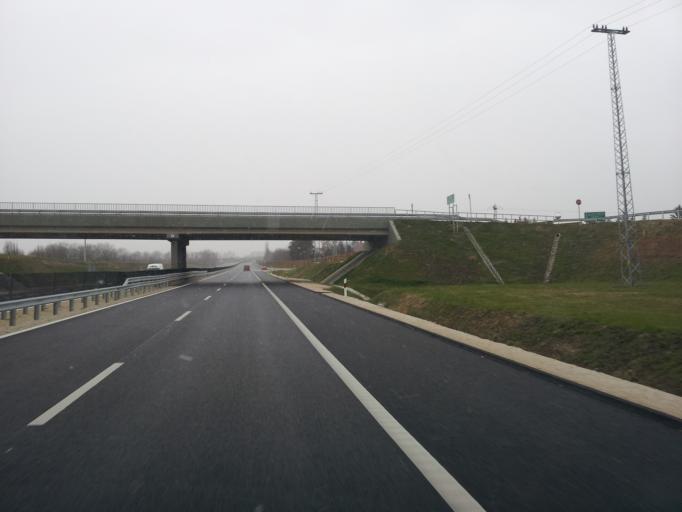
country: HU
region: Veszprem
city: Herend
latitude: 47.1304
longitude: 17.7496
